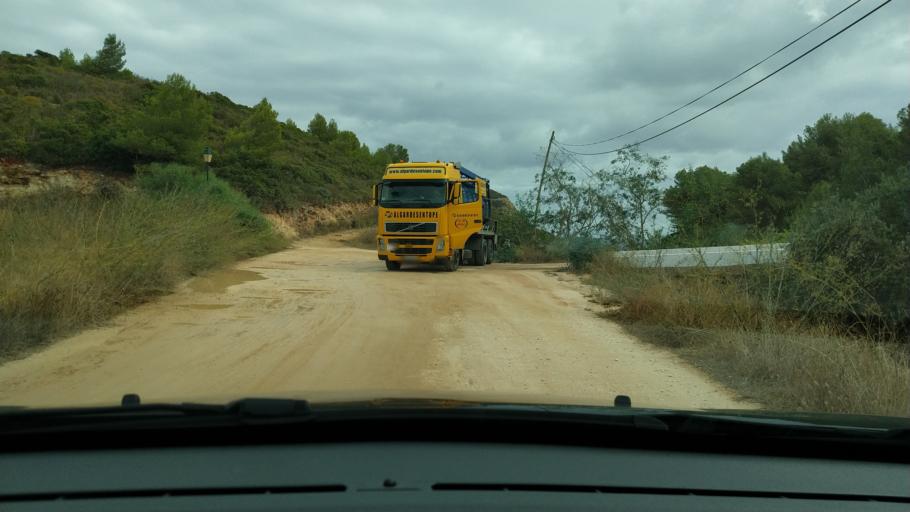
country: PT
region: Faro
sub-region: Vila do Bispo
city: Vila do Bispo
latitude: 37.0680
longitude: -8.7965
